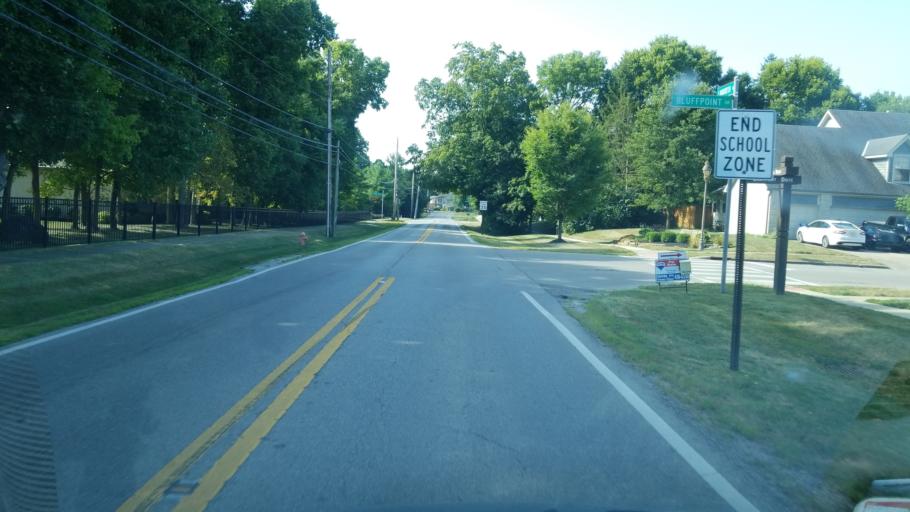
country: US
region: Ohio
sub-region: Franklin County
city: Worthington
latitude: 40.1100
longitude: -83.0426
